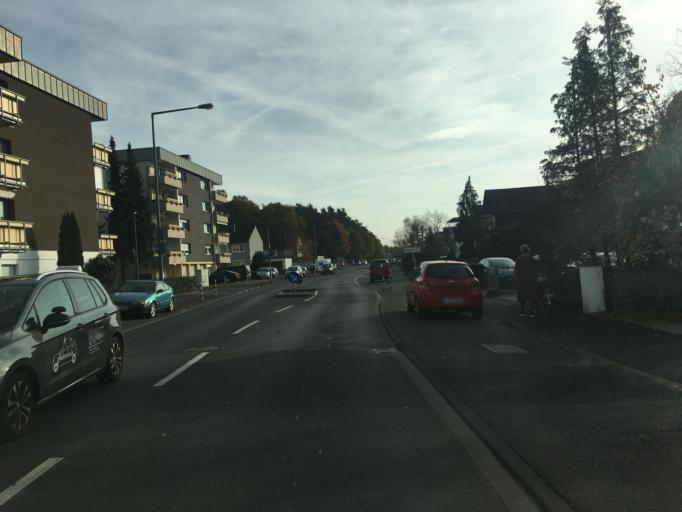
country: DE
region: North Rhine-Westphalia
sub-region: Regierungsbezirk Koln
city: Rath
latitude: 50.9430
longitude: 7.0835
